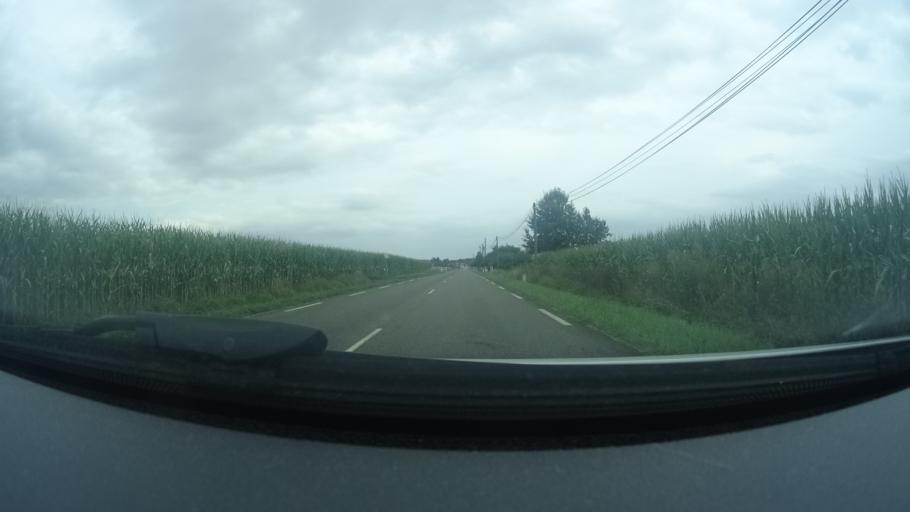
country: FR
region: Aquitaine
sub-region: Departement des Pyrenees-Atlantiques
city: Mont
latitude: 43.4473
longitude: -0.7007
